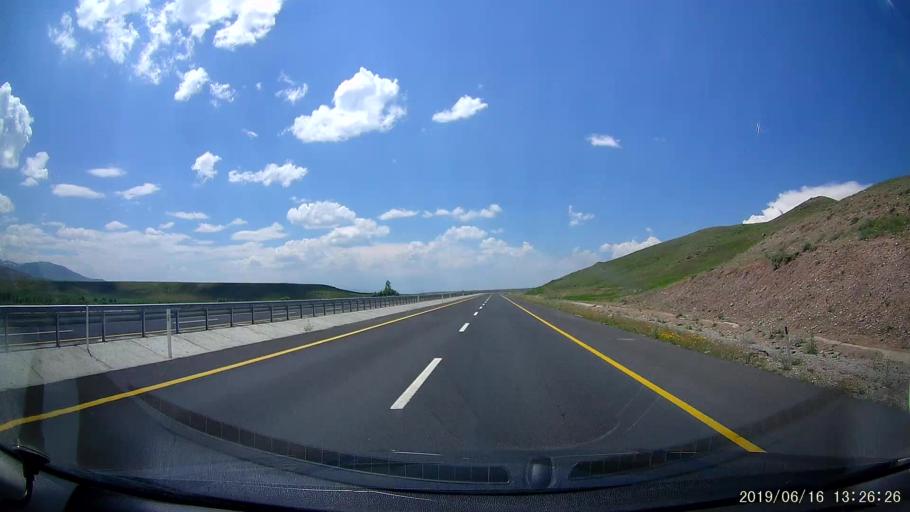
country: TR
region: Agri
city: Taslicay
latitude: 39.6589
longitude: 43.3285
